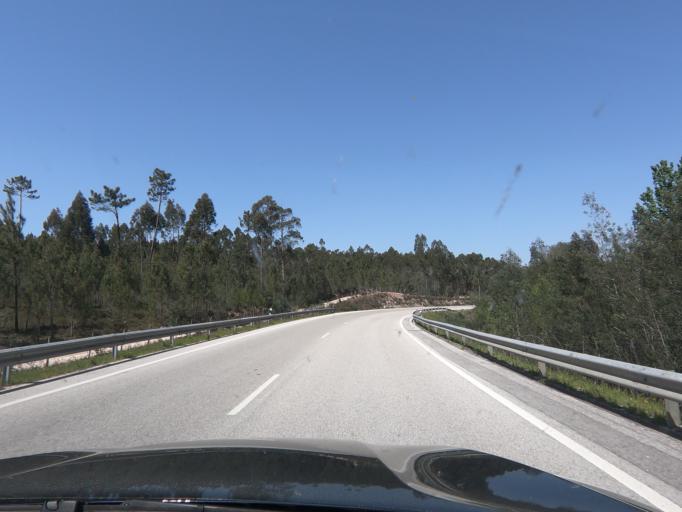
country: PT
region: Coimbra
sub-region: Lousa
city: Lousa
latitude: 40.1222
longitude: -8.2818
